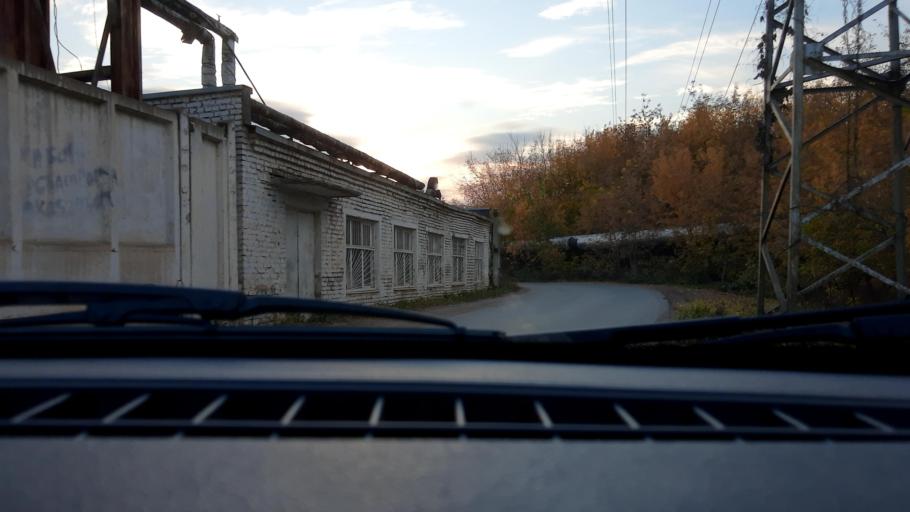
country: RU
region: Bashkortostan
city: Ufa
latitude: 54.7967
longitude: 56.1147
